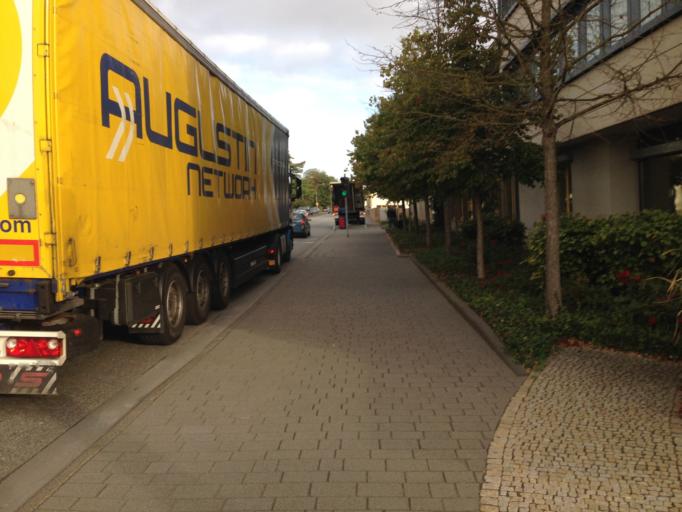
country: DE
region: Hesse
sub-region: Regierungsbezirk Giessen
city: Heuchelheim
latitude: 50.5952
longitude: 8.6299
